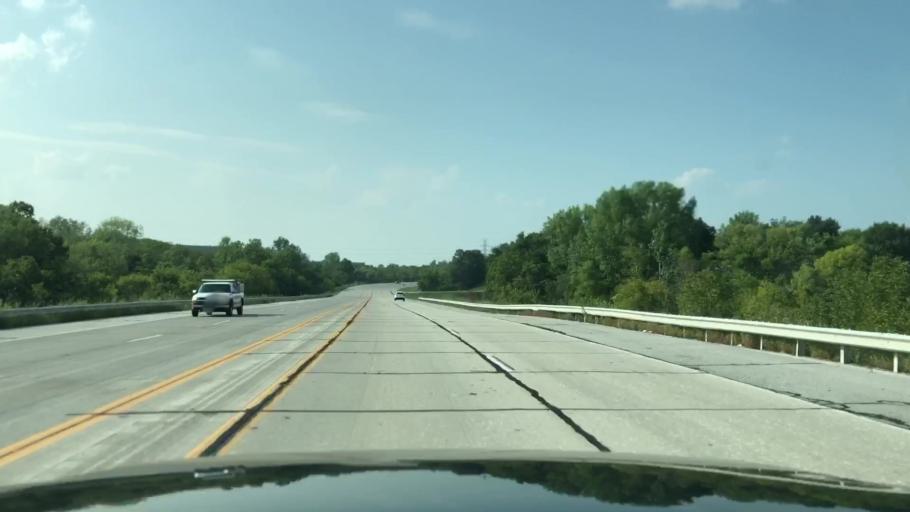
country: US
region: Missouri
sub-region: Saint Charles County
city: Lake Saint Louis
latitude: 38.8102
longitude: -90.8085
